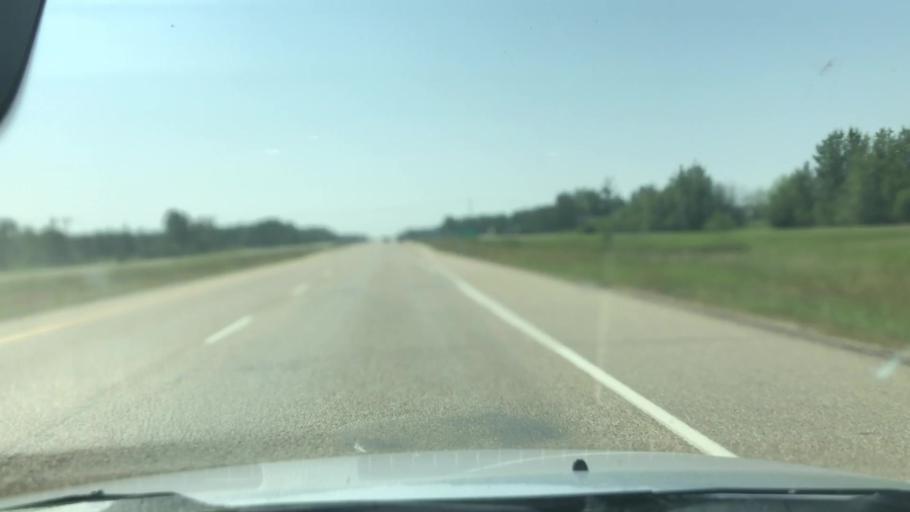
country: CA
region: Alberta
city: Devon
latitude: 53.4277
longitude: -113.7637
